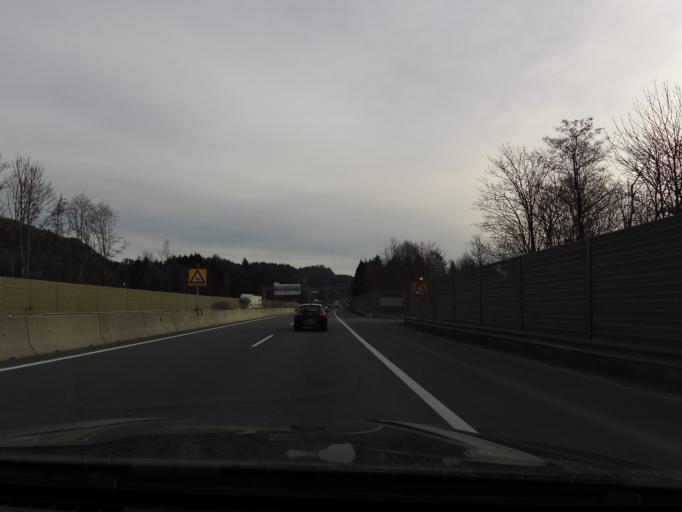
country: AT
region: Tyrol
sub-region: Politischer Bezirk Kufstein
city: Kufstein
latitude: 47.5792
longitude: 12.1496
